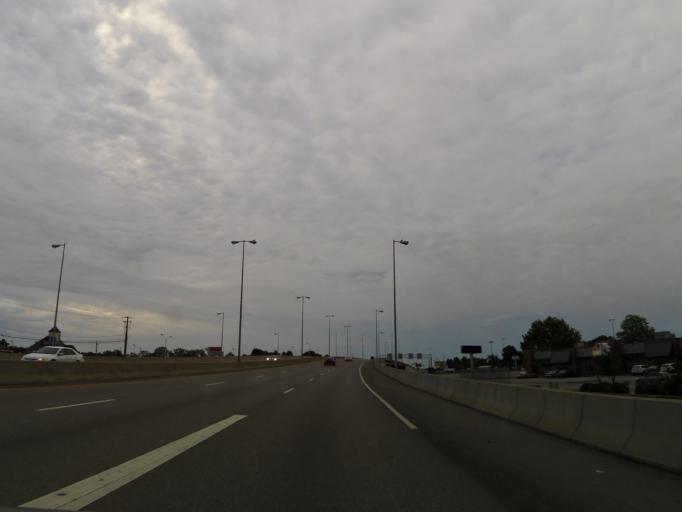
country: US
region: Alabama
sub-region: Madison County
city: Huntsville
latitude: 34.7469
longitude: -86.6001
